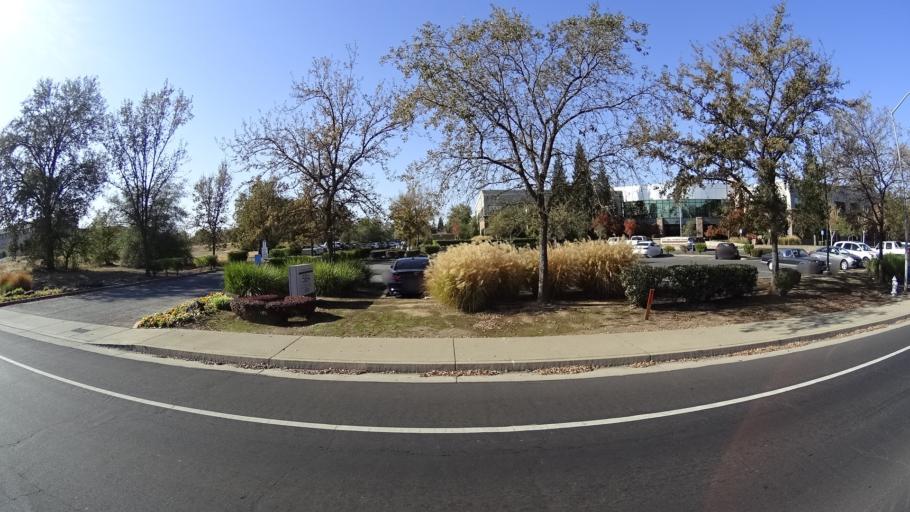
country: US
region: California
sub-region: Sacramento County
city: Citrus Heights
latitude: 38.6828
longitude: -121.2904
